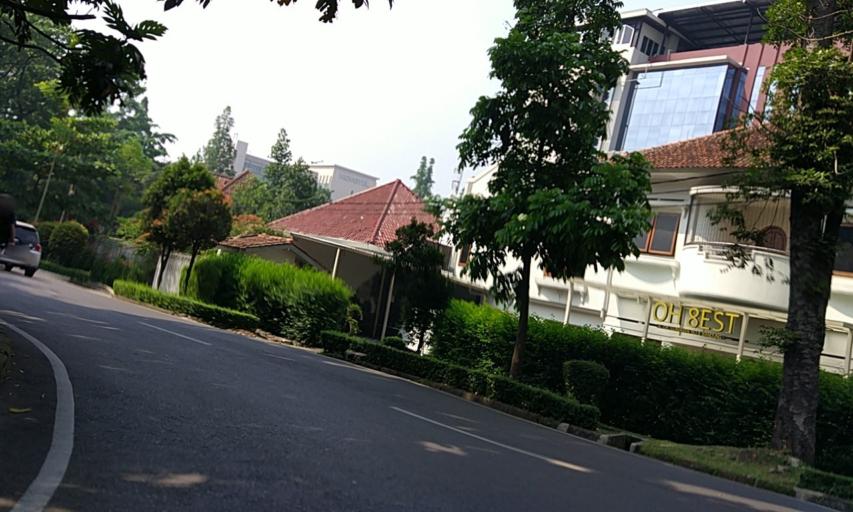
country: ID
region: West Java
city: Bandung
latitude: -6.9038
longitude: 107.6015
